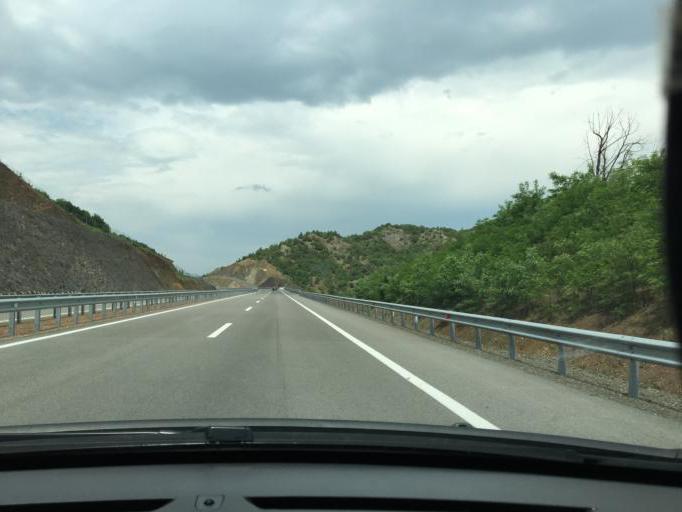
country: MK
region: Gevgelija
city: Miravci
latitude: 41.3554
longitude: 22.3567
